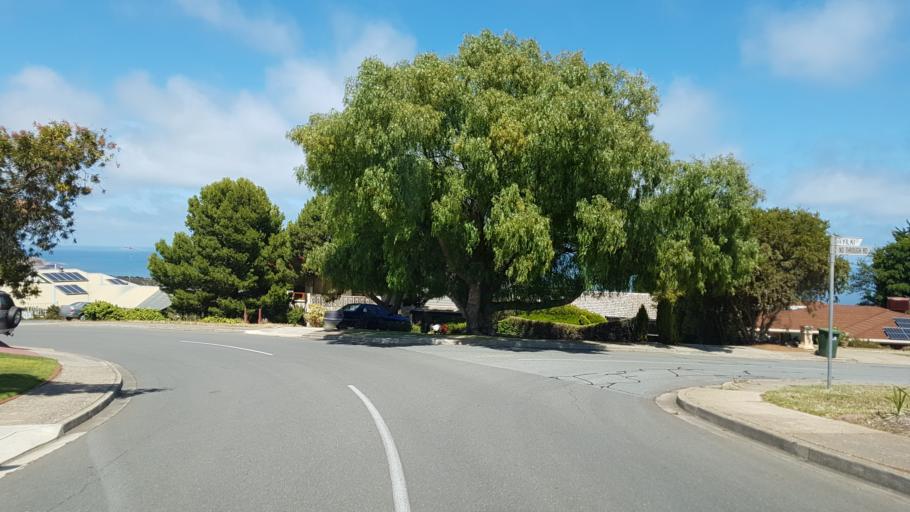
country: AU
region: South Australia
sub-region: Marion
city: Marino
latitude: -35.0682
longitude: 138.5094
